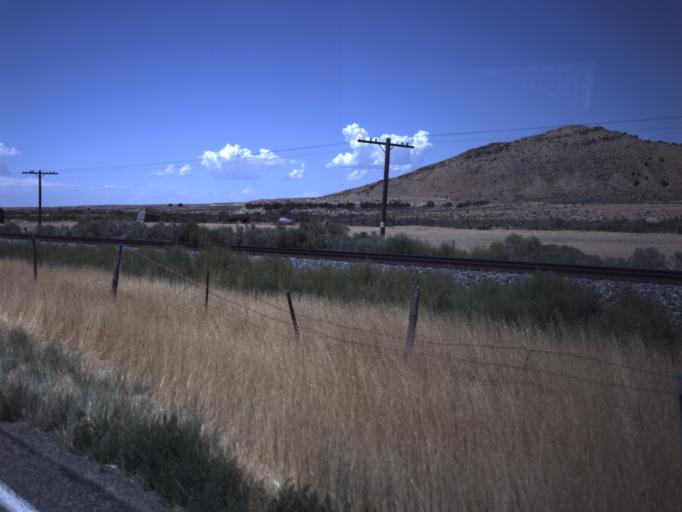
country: US
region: Utah
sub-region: Millard County
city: Delta
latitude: 39.5376
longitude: -112.2611
